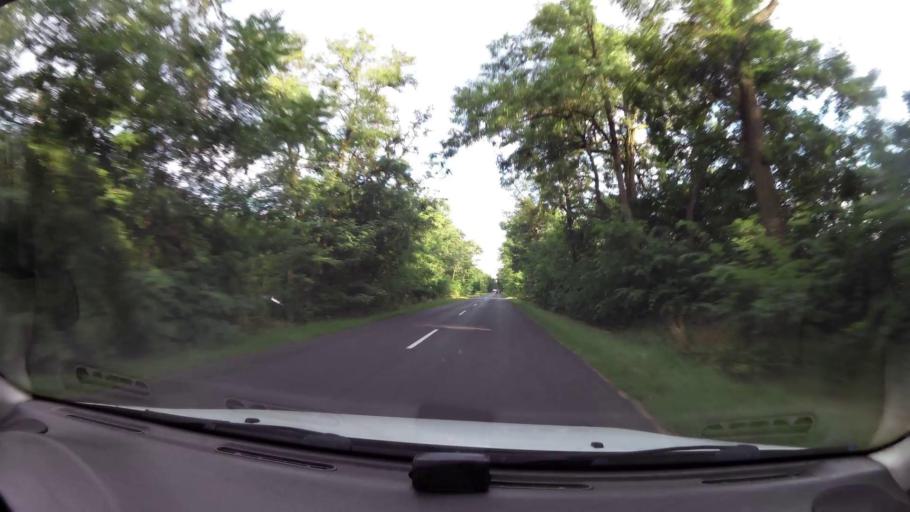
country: HU
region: Pest
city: Tapioszecso
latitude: 47.4304
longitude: 19.6030
